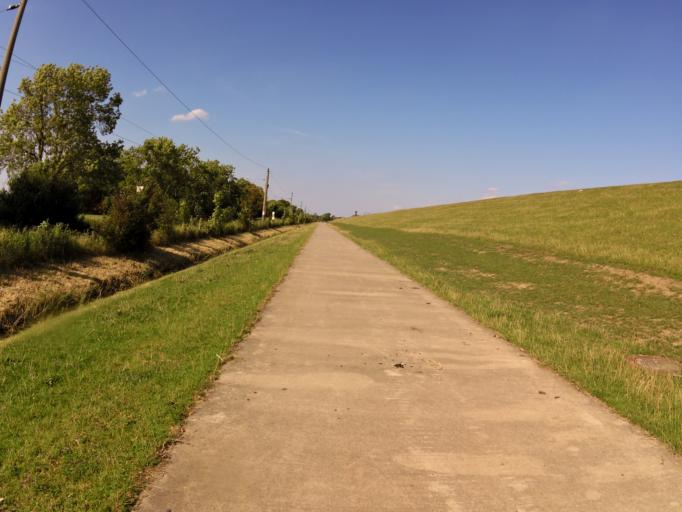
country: DE
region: Lower Saxony
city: Nordenham
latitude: 53.4573
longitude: 8.4749
